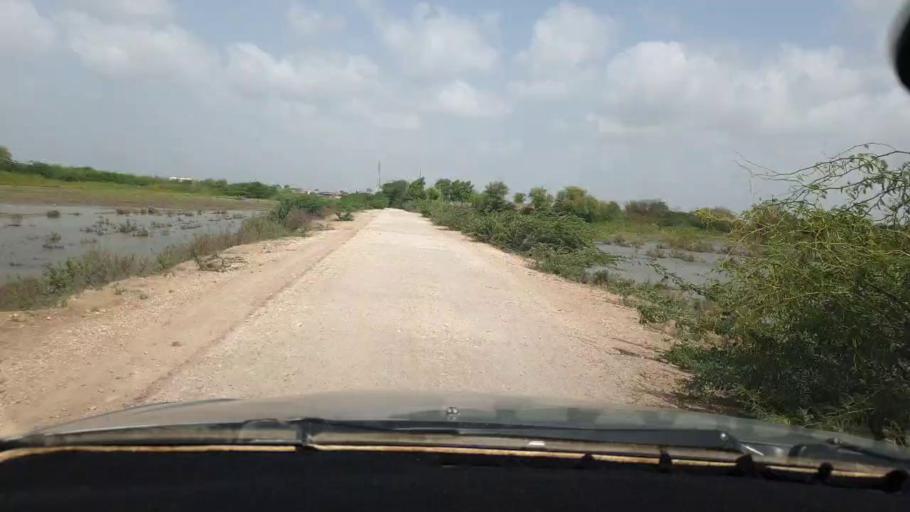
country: PK
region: Sindh
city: Tando Bago
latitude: 24.7552
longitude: 69.1930
